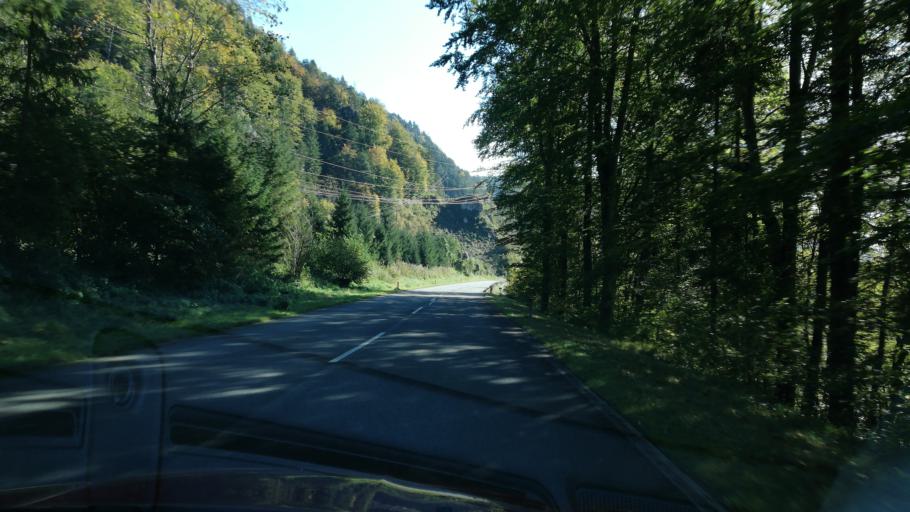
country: AT
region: Styria
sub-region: Politischer Bezirk Liezen
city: Landl
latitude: 47.6963
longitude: 14.6859
